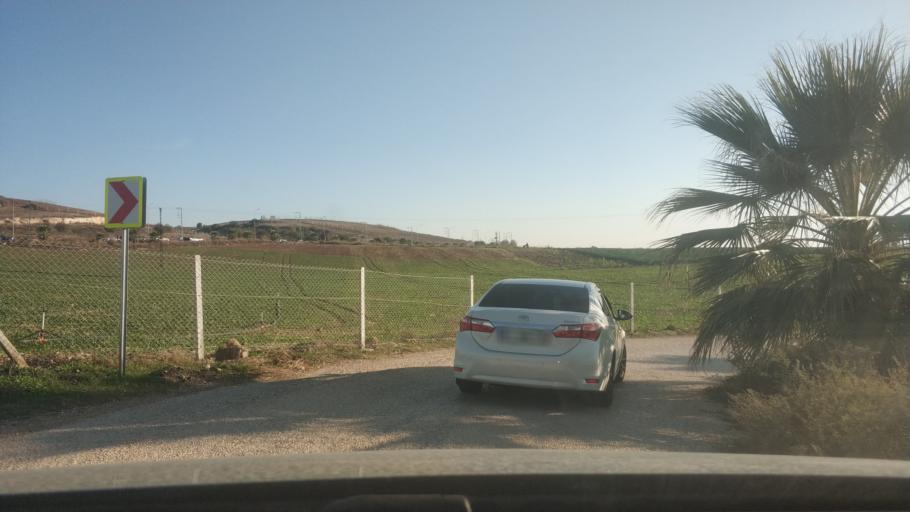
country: TR
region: Adana
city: Adana
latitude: 37.0968
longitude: 35.3034
